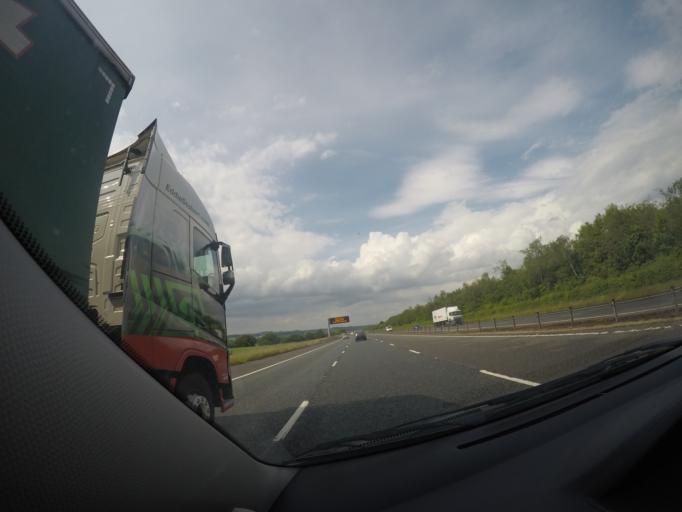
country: GB
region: Scotland
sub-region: Dumfries and Galloway
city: Lochmaben
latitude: 55.1839
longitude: -3.4064
